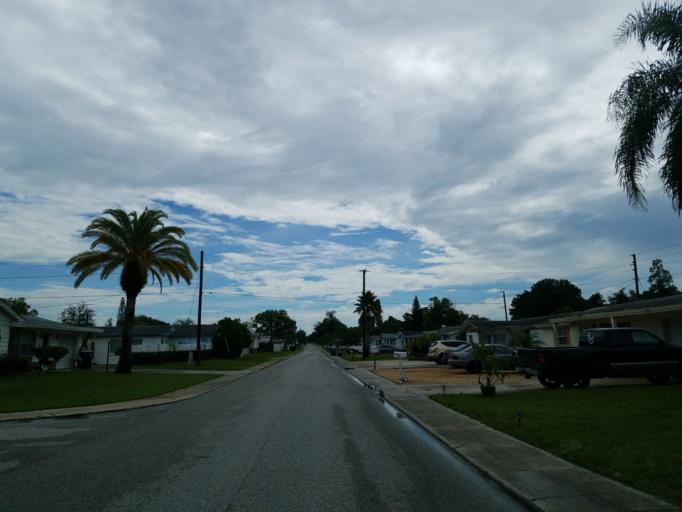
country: US
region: Florida
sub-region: Pasco County
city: Beacon Square
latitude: 28.2062
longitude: -82.7513
